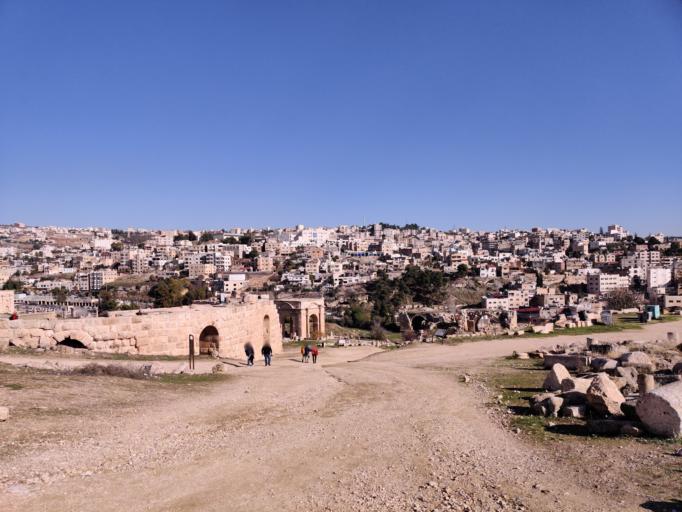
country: JO
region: Jerash
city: Jarash
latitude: 32.2822
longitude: 35.8918
